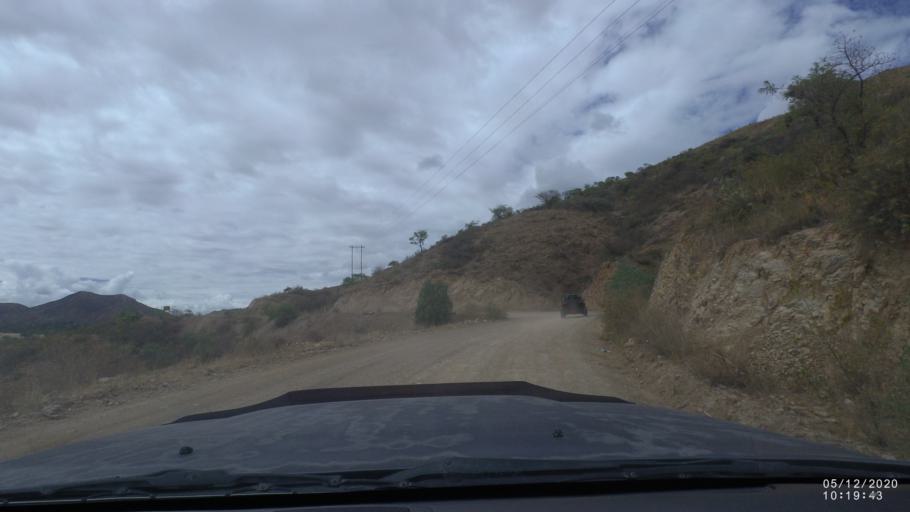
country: BO
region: Cochabamba
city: Sipe Sipe
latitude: -17.4799
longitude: -66.2831
